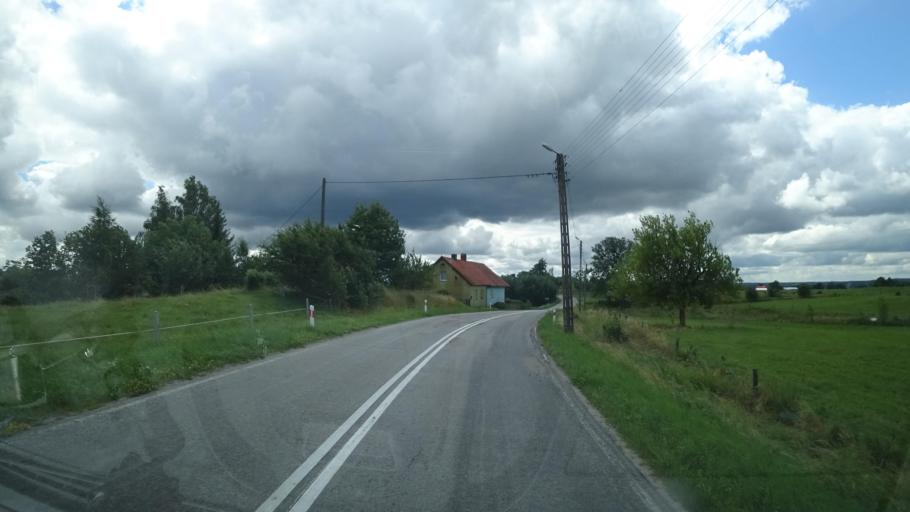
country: PL
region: Warmian-Masurian Voivodeship
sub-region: Powiat goldapski
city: Goldap
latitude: 54.2216
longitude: 22.2322
